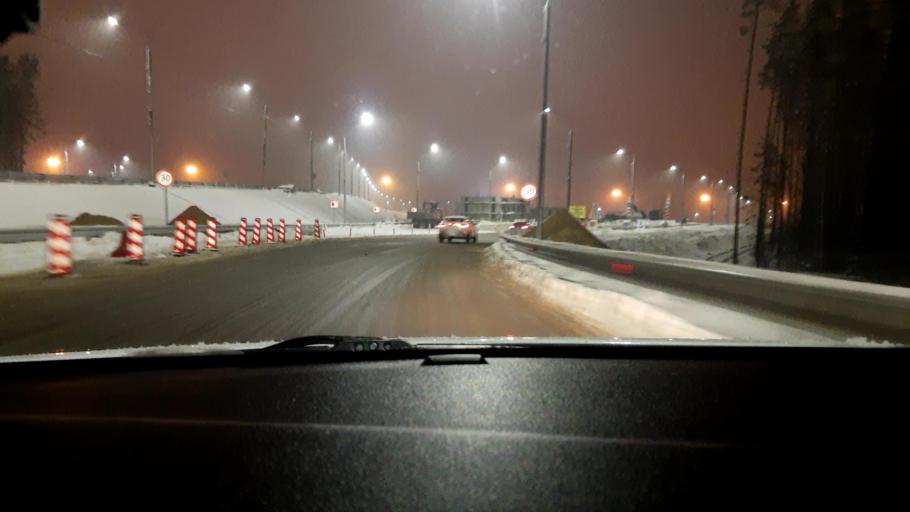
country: RU
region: Moskovskaya
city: Nemchinovka
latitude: 55.7091
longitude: 37.3180
